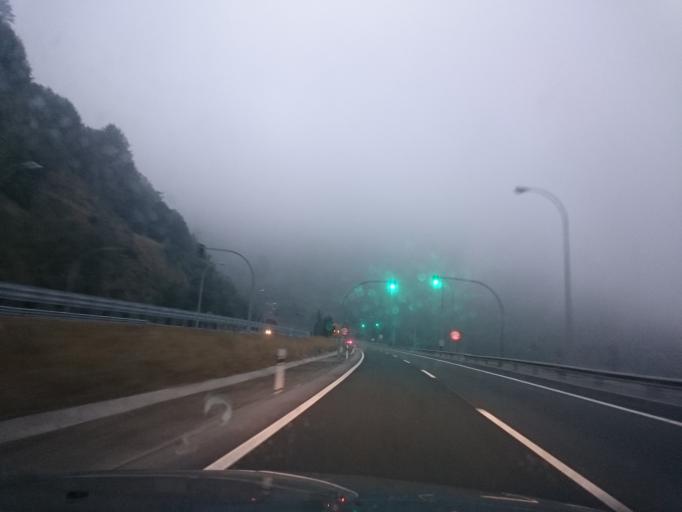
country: ES
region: Castille and Leon
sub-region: Provincia de Leon
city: Sena de Luna
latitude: 42.9922
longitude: -5.8161
